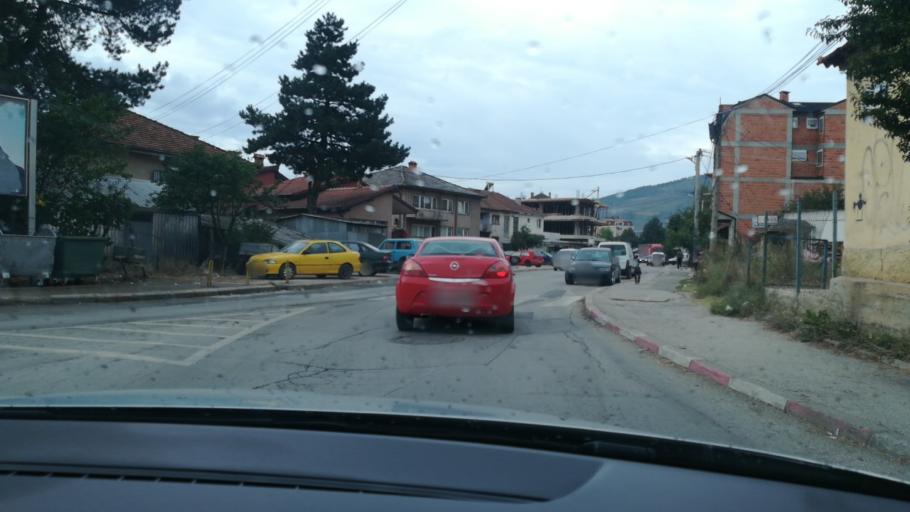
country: MK
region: Kicevo
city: Kicevo
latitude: 41.5090
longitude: 20.9585
